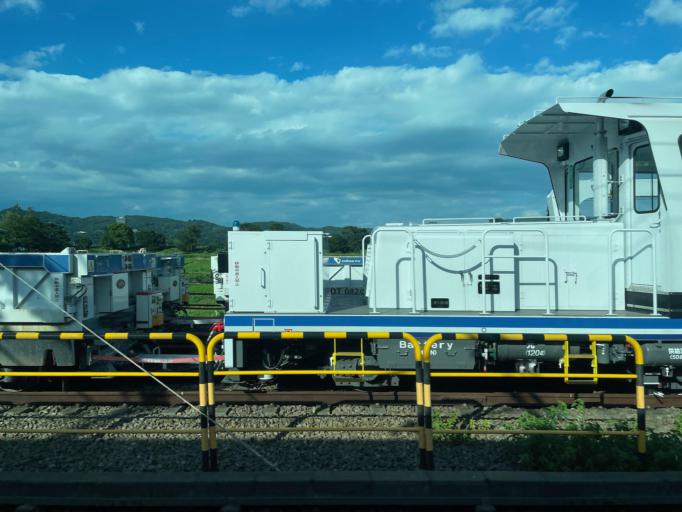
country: JP
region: Kanagawa
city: Odawara
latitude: 35.3223
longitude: 139.1378
